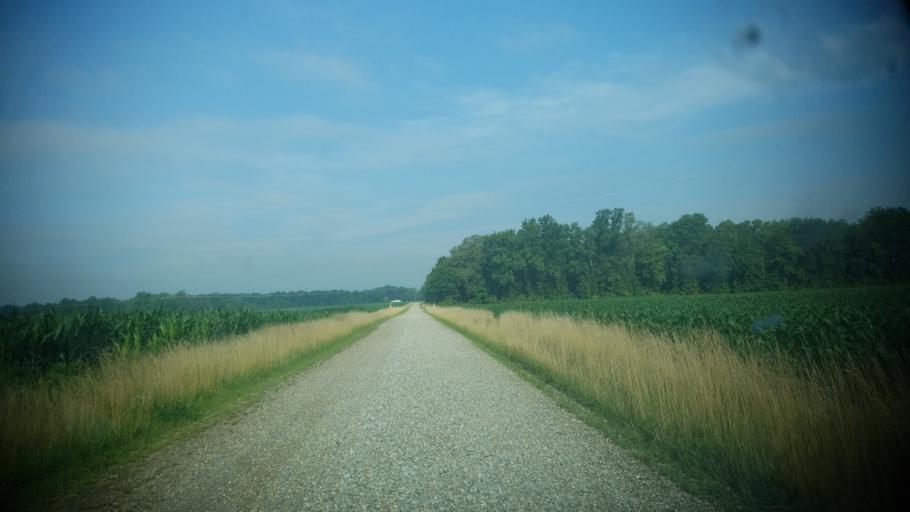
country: US
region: Illinois
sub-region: Clay County
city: Flora
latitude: 38.6019
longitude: -88.3562
